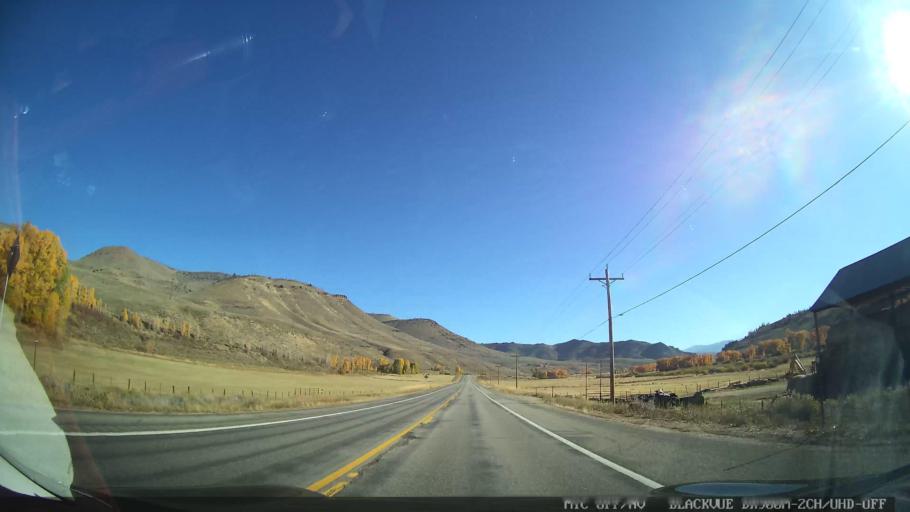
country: US
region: Colorado
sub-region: Grand County
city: Hot Sulphur Springs
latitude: 40.1007
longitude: -106.0304
